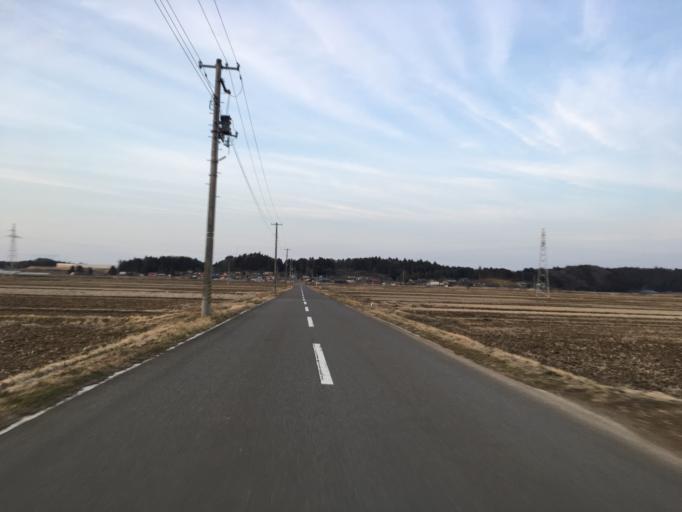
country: JP
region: Fukushima
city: Ishikawa
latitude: 37.0566
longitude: 140.3474
